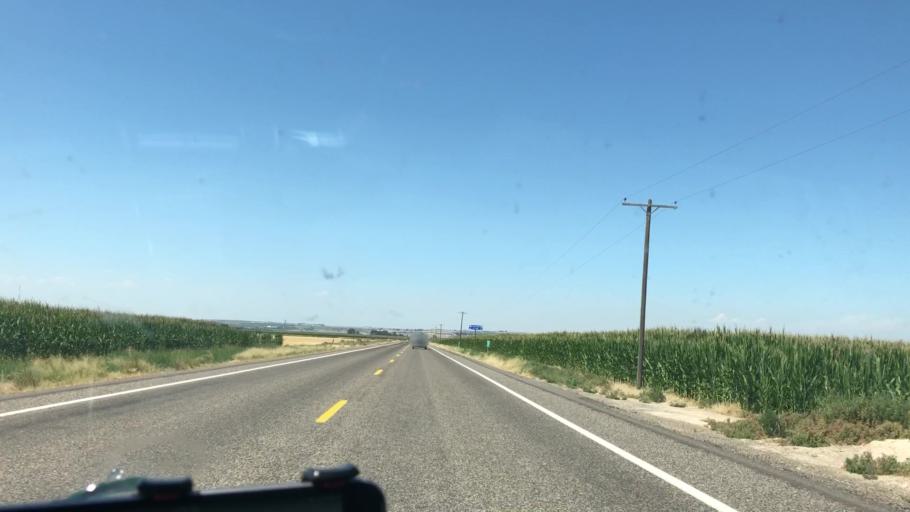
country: US
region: Idaho
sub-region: Owyhee County
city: Marsing
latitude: 43.5263
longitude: -116.8516
